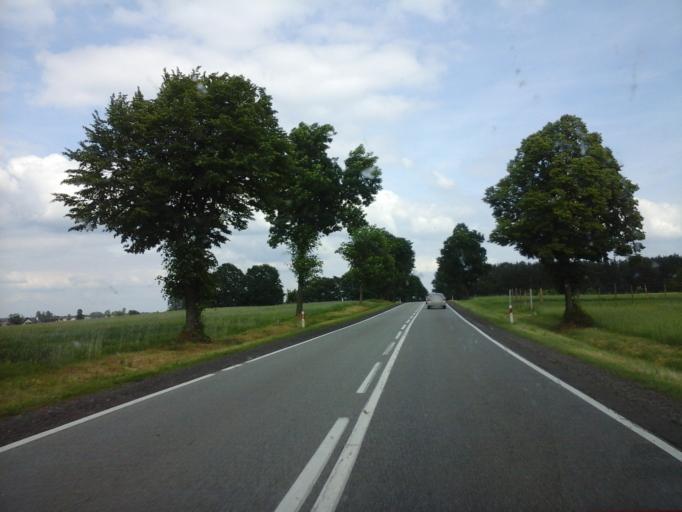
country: PL
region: Lodz Voivodeship
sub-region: Powiat opoczynski
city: Paradyz
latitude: 51.3128
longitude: 20.0794
